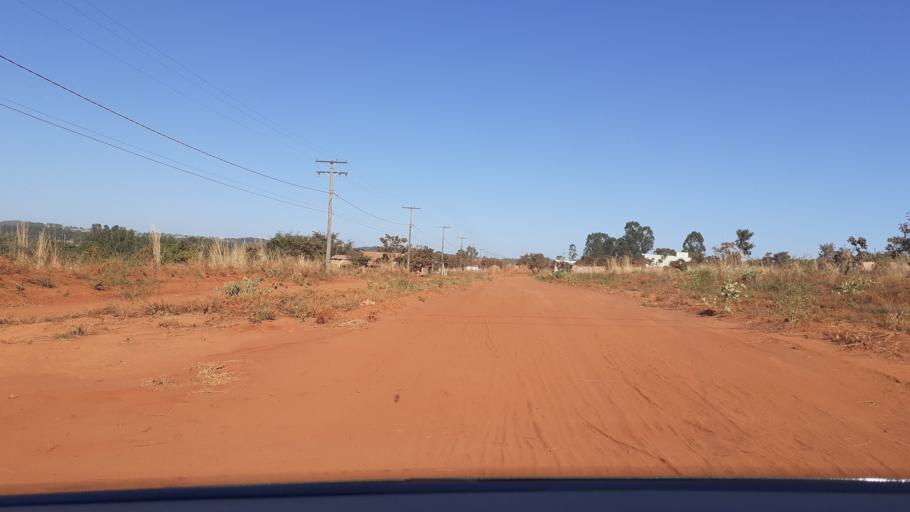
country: BR
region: Goias
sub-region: Aparecida De Goiania
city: Aparecida de Goiania
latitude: -16.8732
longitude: -49.2747
